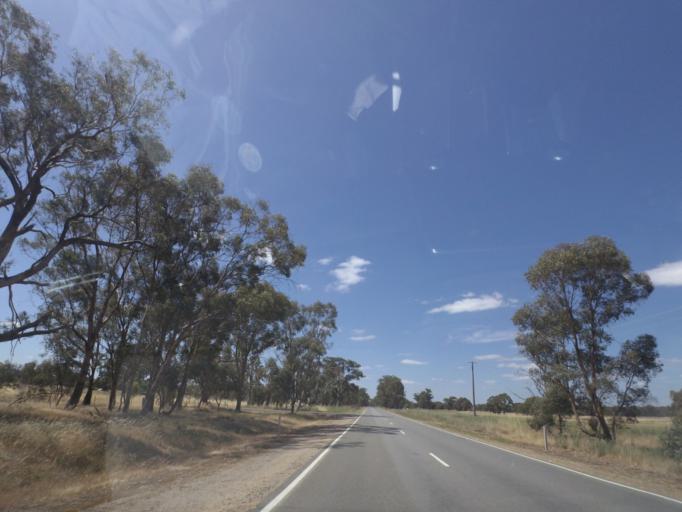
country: AU
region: Victoria
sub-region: Wangaratta
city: Wangaratta
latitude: -36.4171
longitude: 146.2641
